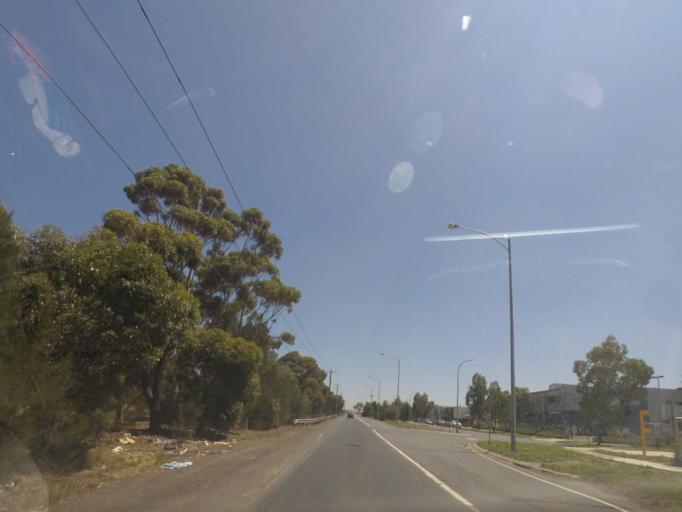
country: AU
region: Victoria
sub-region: Hume
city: Craigieburn
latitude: -37.6038
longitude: 144.9465
